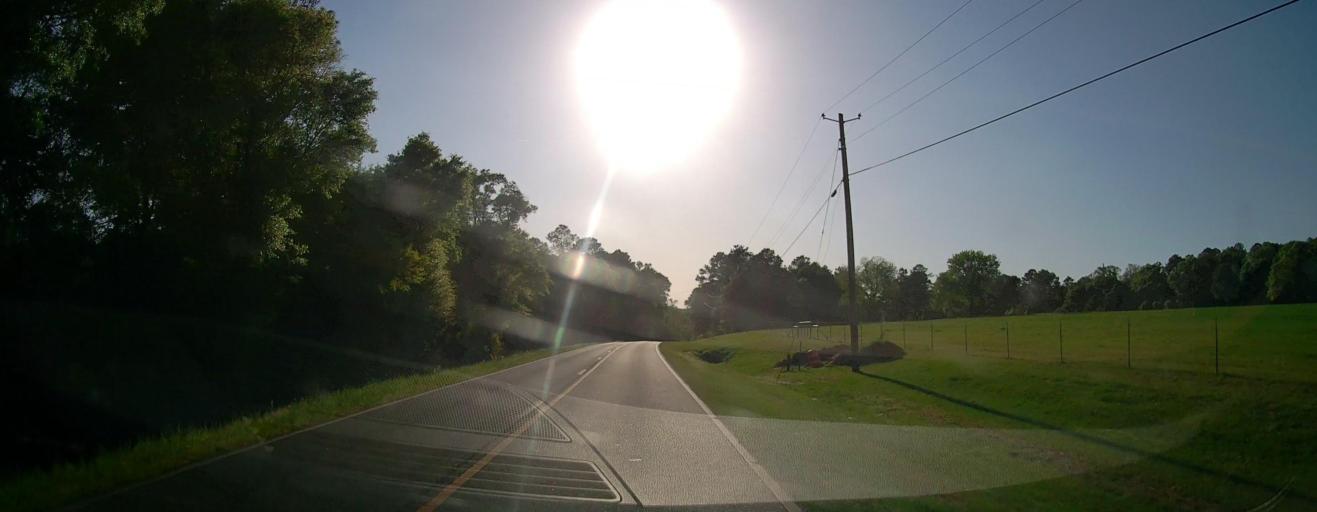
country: US
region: Georgia
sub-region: Macon County
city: Montezuma
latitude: 32.3140
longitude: -84.0028
